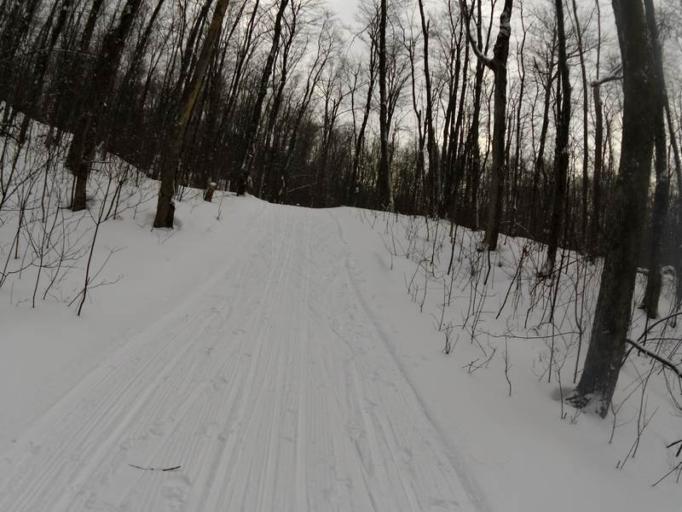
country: CA
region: Quebec
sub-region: Outaouais
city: Wakefield
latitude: 45.5288
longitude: -75.9191
